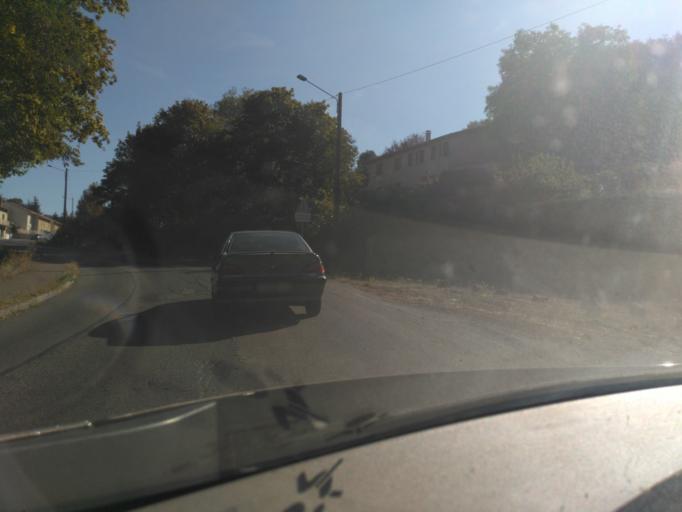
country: FR
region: Rhone-Alpes
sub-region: Departement du Rhone
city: Tarare
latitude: 45.8913
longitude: 4.4339
